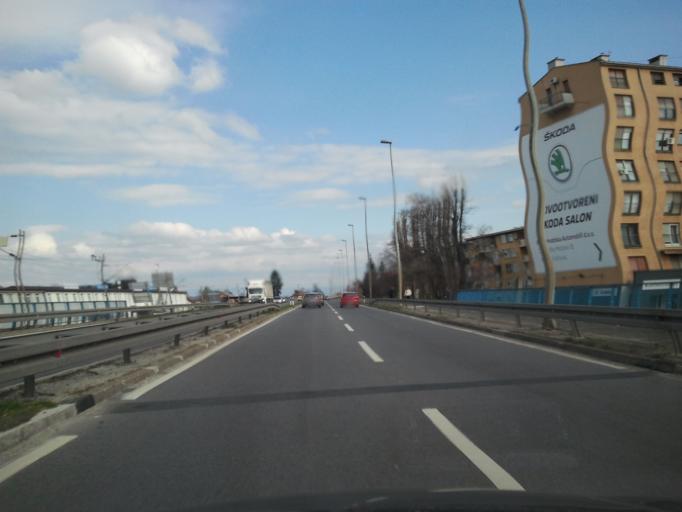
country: HR
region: Karlovacka
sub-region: Grad Karlovac
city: Karlovac
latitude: 45.4913
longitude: 15.5476
